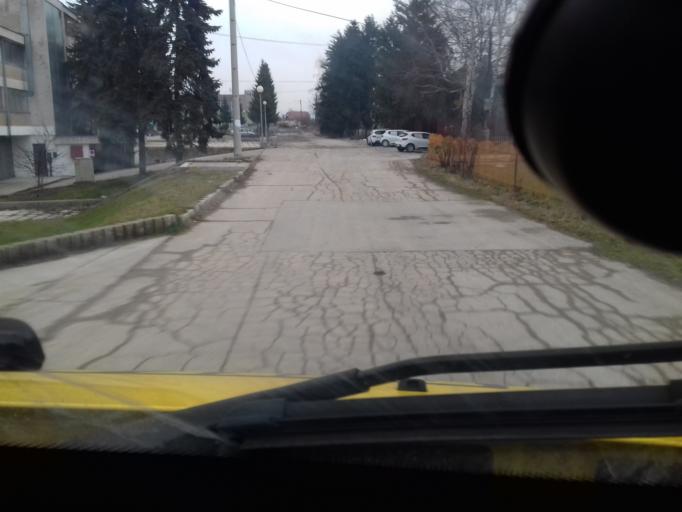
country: BA
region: Federation of Bosnia and Herzegovina
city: Zenica
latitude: 44.1927
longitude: 17.9285
